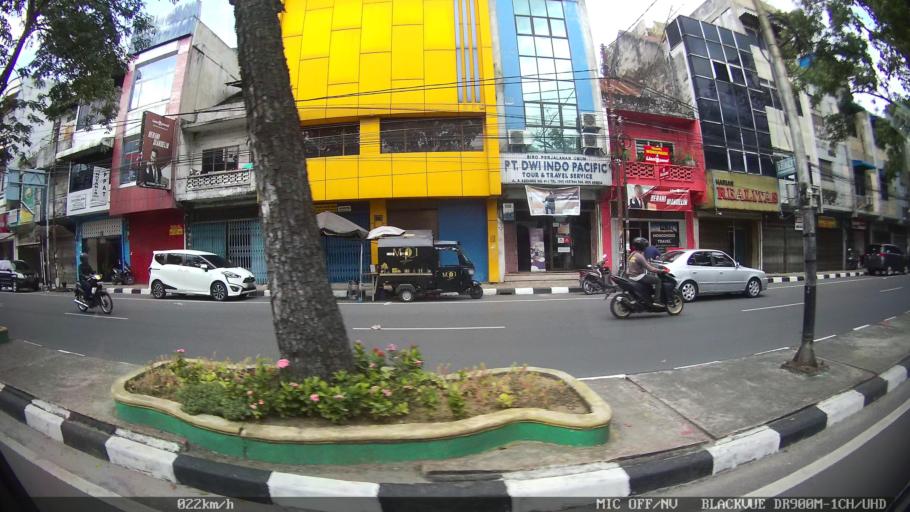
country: ID
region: North Sumatra
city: Medan
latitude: 3.5780
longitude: 98.6846
